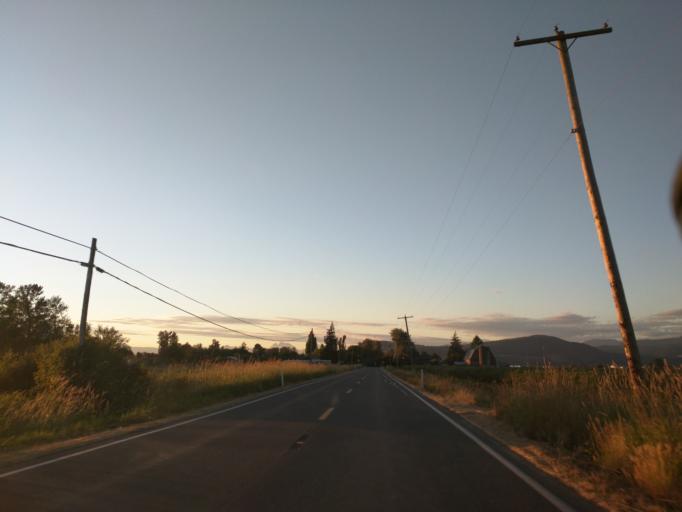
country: US
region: Washington
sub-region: Whatcom County
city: Sumas
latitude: 48.9889
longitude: -122.2477
